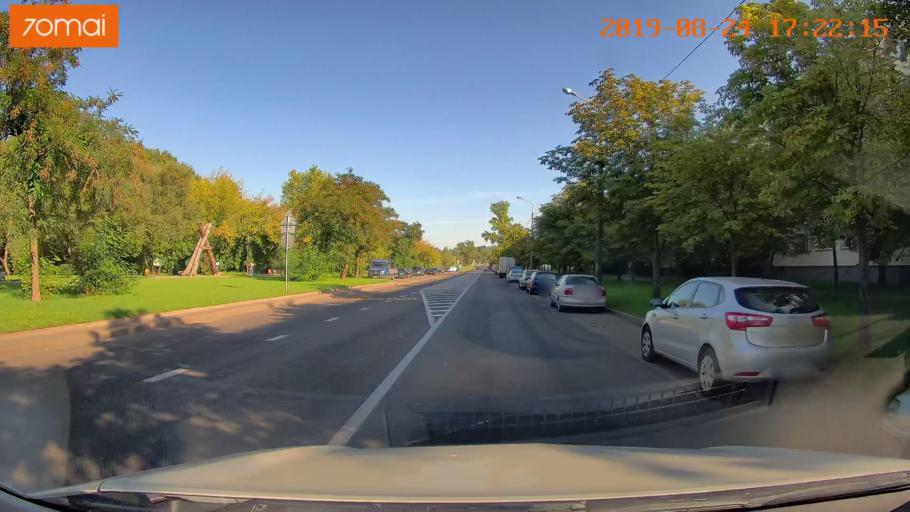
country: BY
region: Minsk
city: Hatava
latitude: 53.8468
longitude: 27.6423
